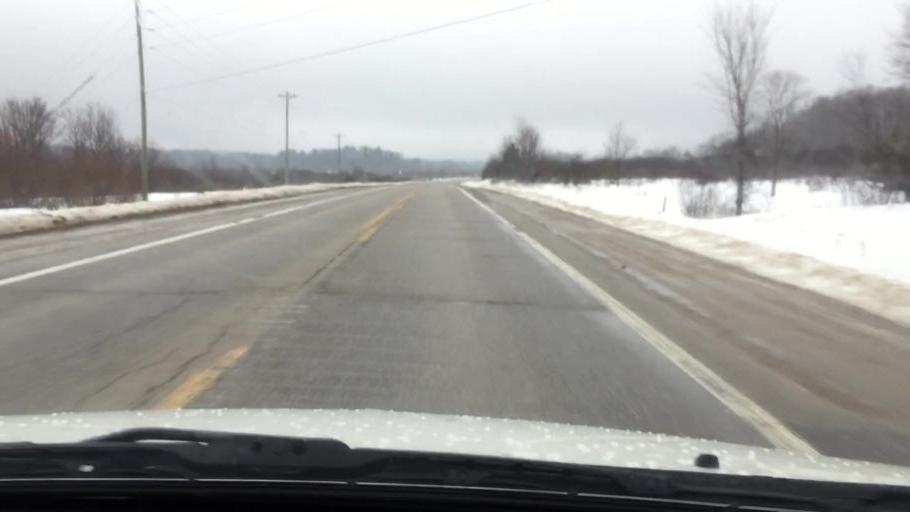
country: US
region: Michigan
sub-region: Charlevoix County
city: East Jordan
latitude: 45.1250
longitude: -85.1338
